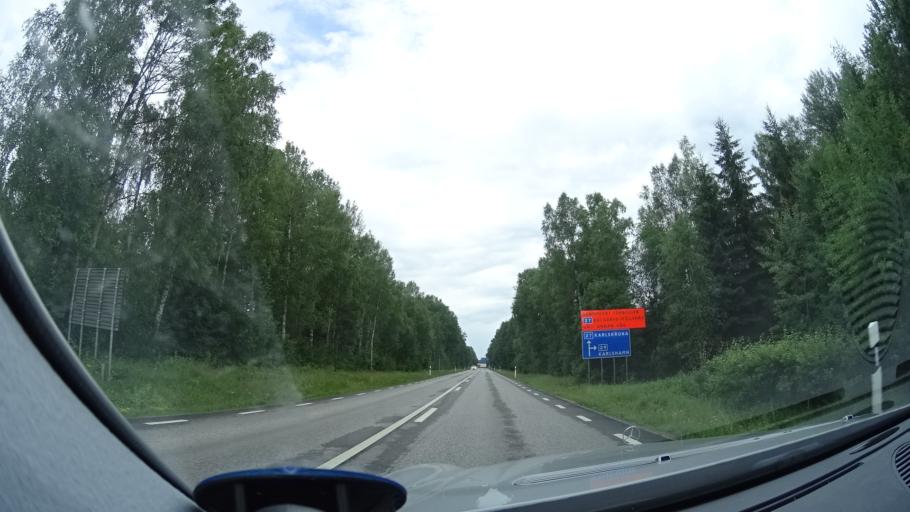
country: SE
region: Kronoberg
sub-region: Tingsryds Kommun
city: Tingsryd
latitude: 56.4719
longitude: 15.0078
